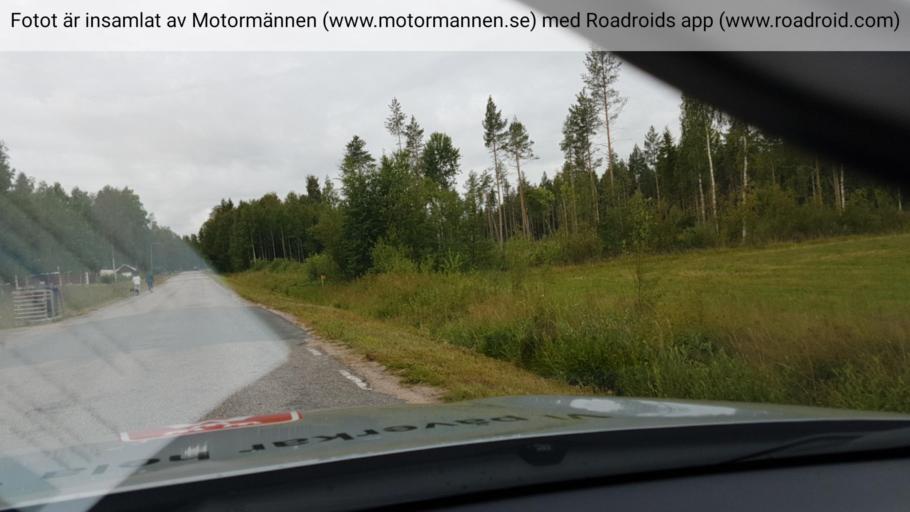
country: SE
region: Norrbotten
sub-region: Bodens Kommun
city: Saevast
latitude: 65.6726
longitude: 21.7906
